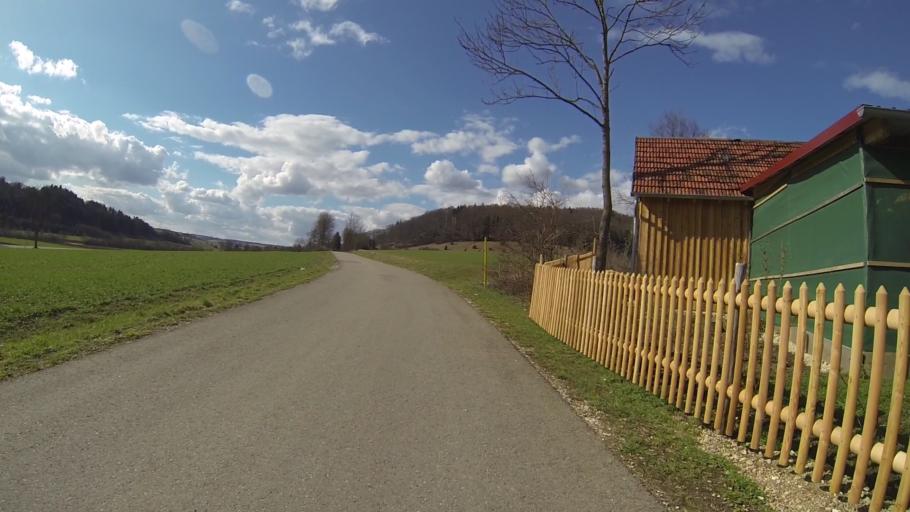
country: DE
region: Baden-Wuerttemberg
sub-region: Regierungsbezirk Stuttgart
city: Steinheim am Albuch
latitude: 48.6820
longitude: 10.0988
